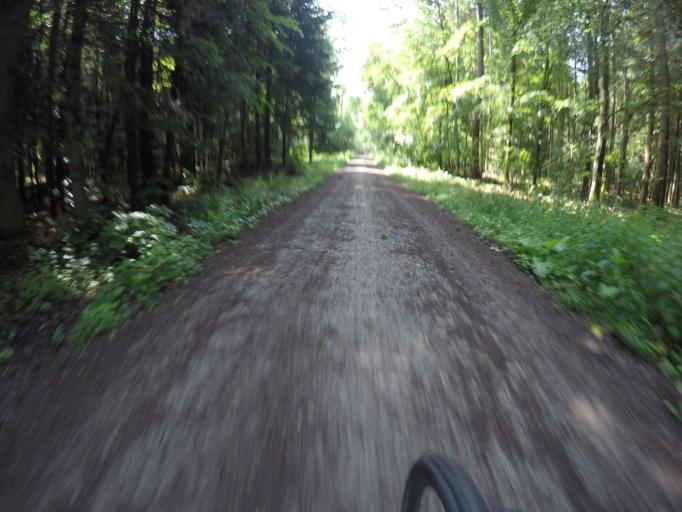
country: DE
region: Baden-Wuerttemberg
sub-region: Regierungsbezirk Stuttgart
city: Nufringen
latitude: 48.6327
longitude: 8.8588
